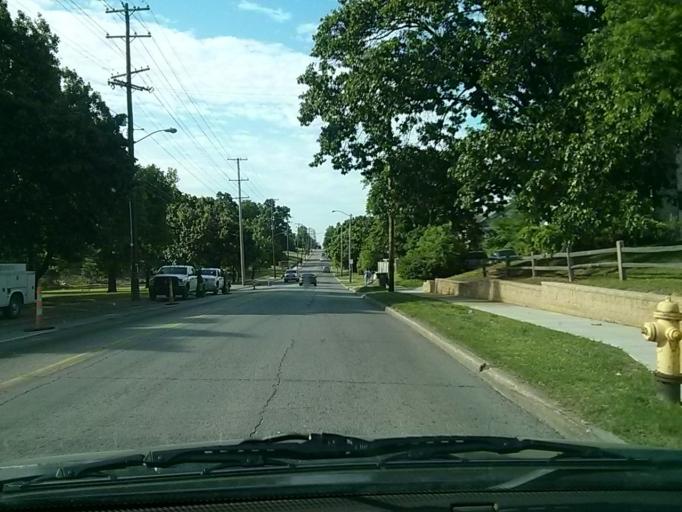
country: US
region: Oklahoma
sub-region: Tulsa County
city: Tulsa
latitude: 36.1333
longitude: -95.9757
